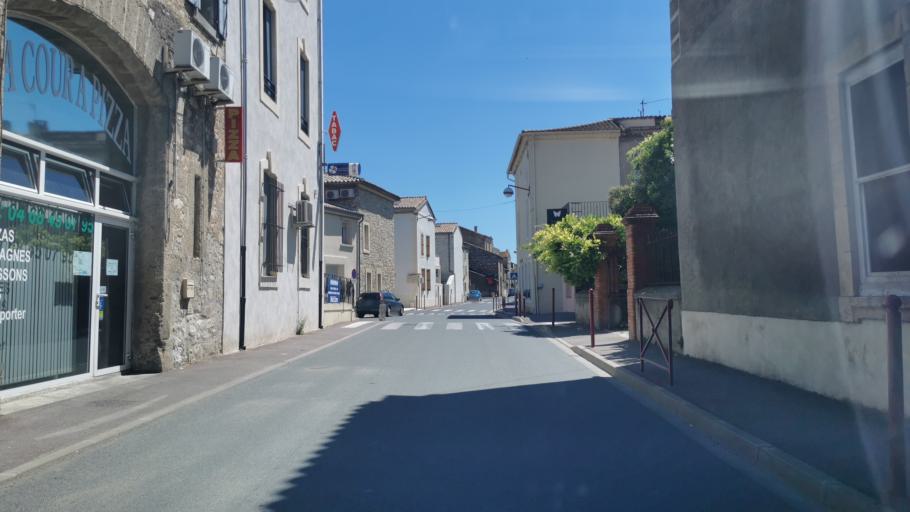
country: FR
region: Languedoc-Roussillon
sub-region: Departement de l'Aude
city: Vinassan
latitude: 43.2041
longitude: 3.0746
